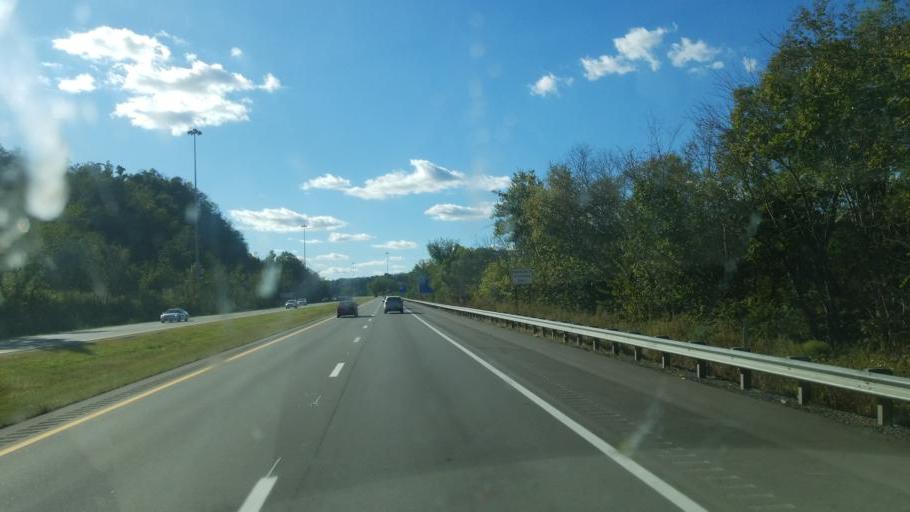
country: US
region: West Virginia
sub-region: Ohio County
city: Bethlehem
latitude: 40.0457
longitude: -80.6349
